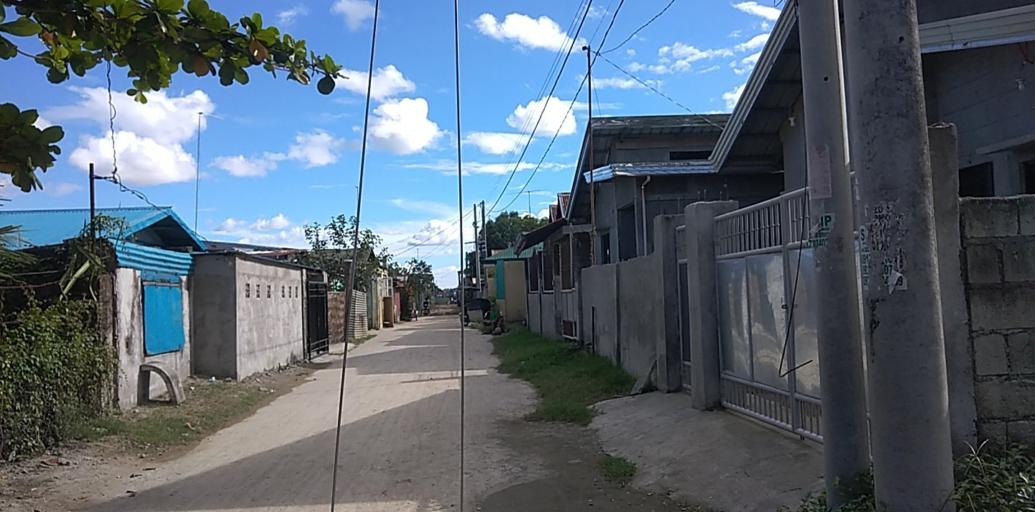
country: PH
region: Central Luzon
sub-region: Province of Pampanga
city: Arayat
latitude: 15.1369
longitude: 120.7709
